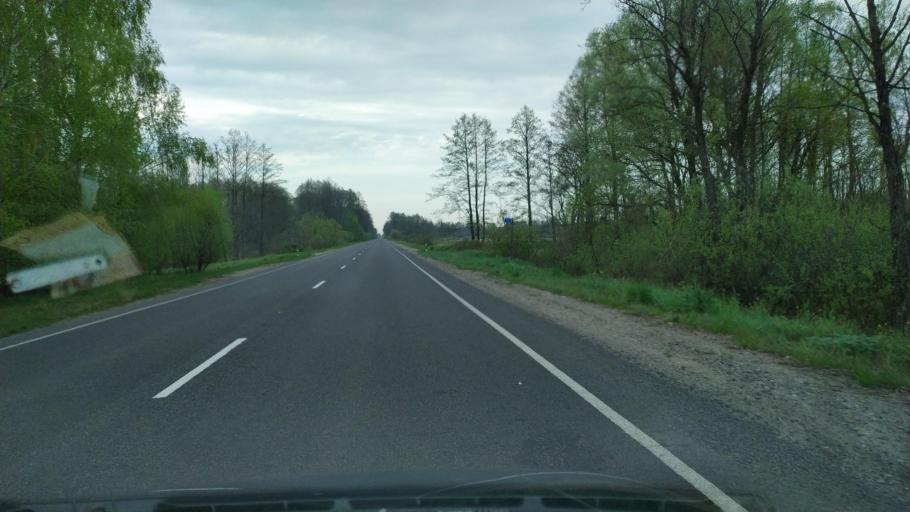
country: BY
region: Brest
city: Zhabinka
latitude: 52.2758
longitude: 23.9519
